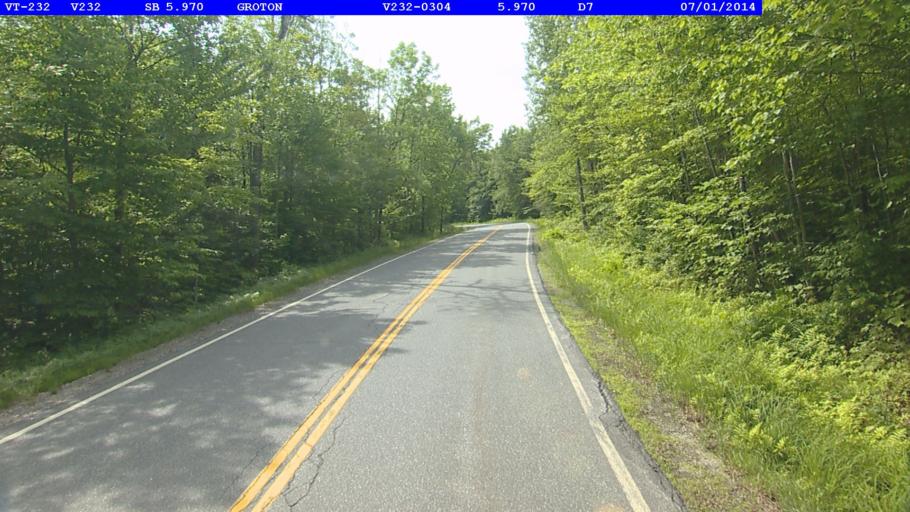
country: US
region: Vermont
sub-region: Washington County
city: Barre
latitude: 44.2823
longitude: -72.2932
